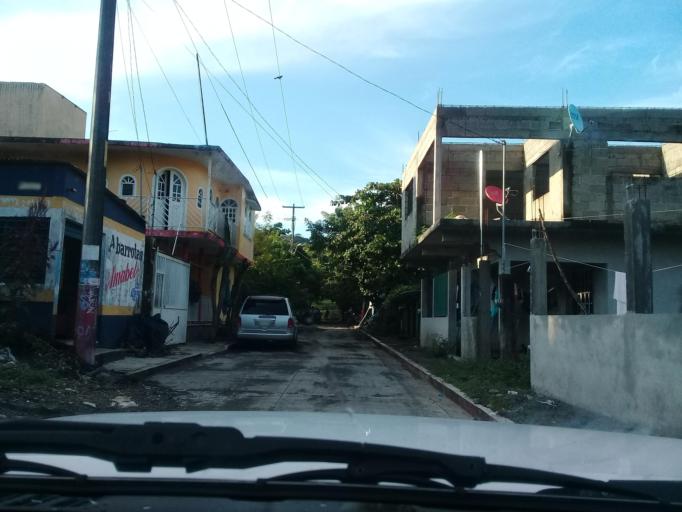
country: MX
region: Veracruz
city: Catemaco
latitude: 18.4241
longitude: -95.0994
